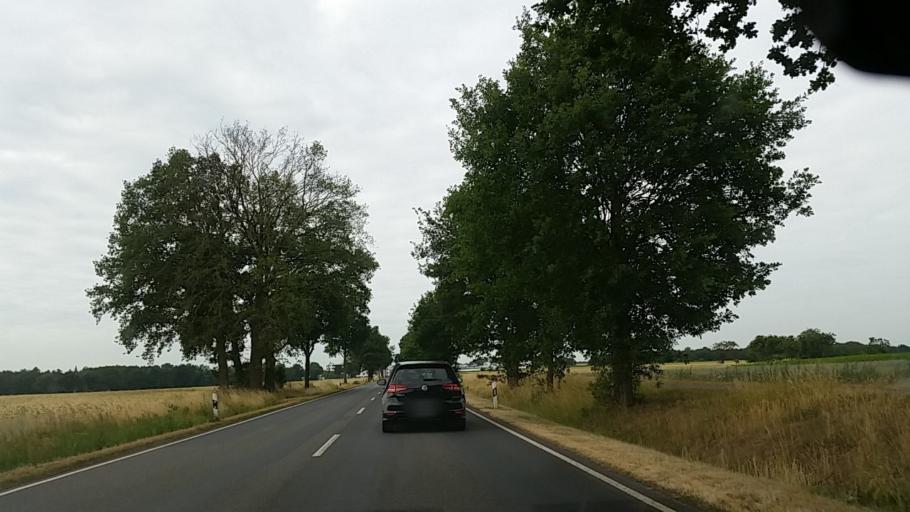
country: DE
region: Lower Saxony
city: Tappenbeck
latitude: 52.4871
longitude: 10.7463
